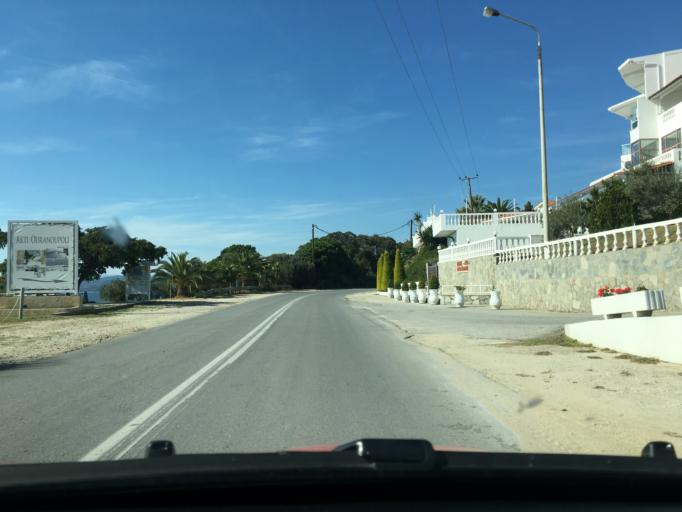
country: GR
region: Central Macedonia
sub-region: Nomos Chalkidikis
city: Ouranoupolis
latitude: 40.3470
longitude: 23.9636
